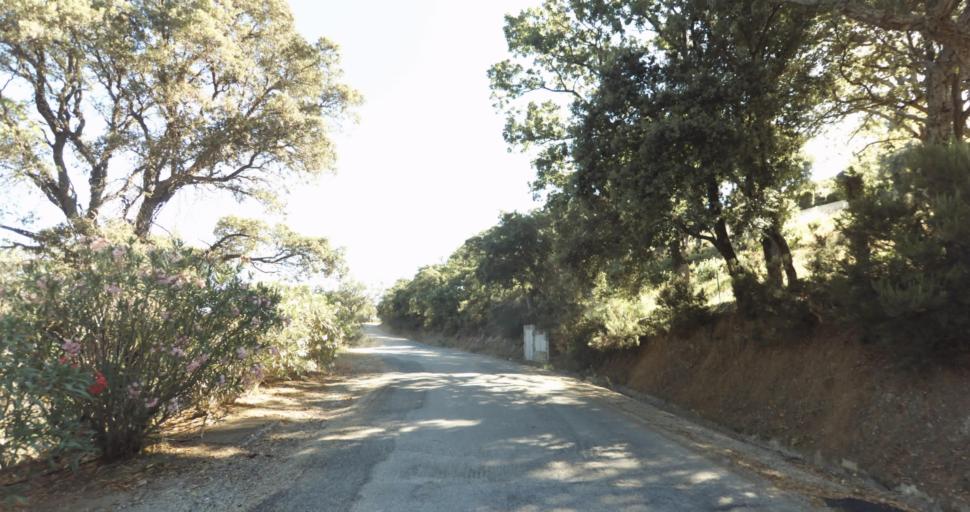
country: FR
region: Provence-Alpes-Cote d'Azur
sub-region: Departement du Var
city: Gassin
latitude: 43.2210
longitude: 6.5952
